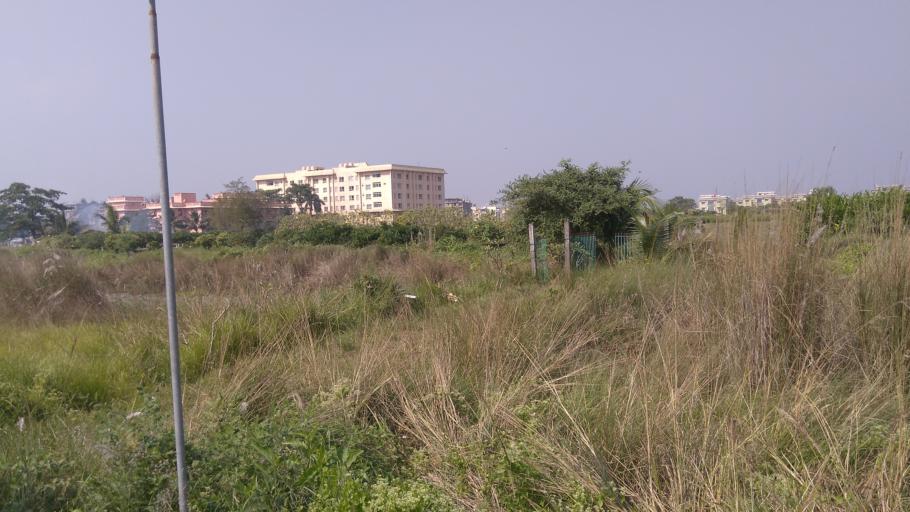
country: IN
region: West Bengal
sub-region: Nadia
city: Navadwip
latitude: 23.4257
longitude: 88.3935
